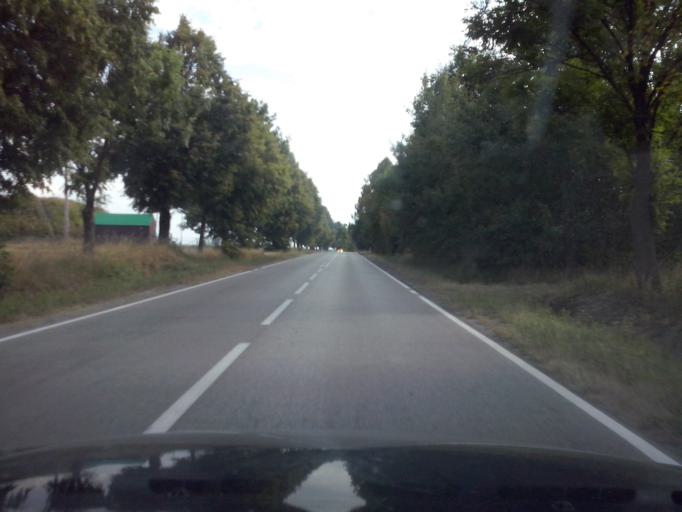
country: PL
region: Swietokrzyskie
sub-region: Powiat kielecki
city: Rakow
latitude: 50.6923
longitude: 21.0596
